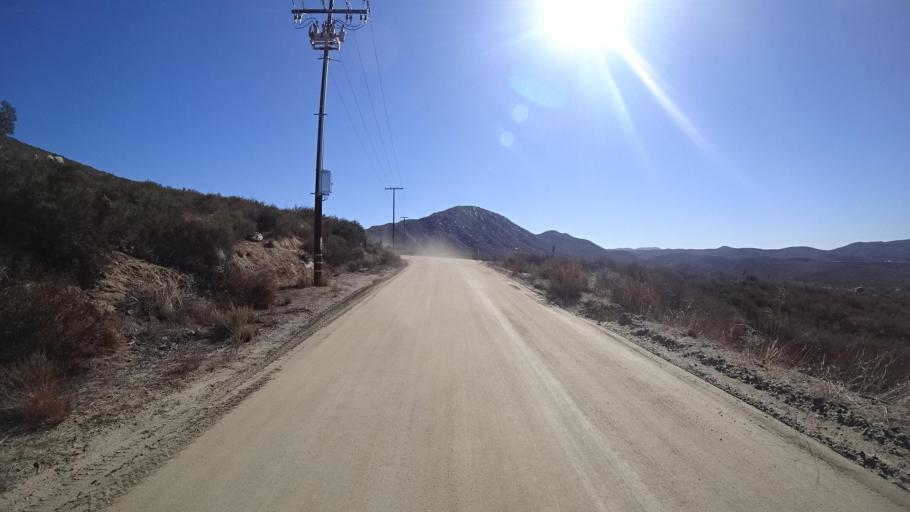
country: US
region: California
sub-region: San Diego County
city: Descanso
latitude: 32.8594
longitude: -116.6826
